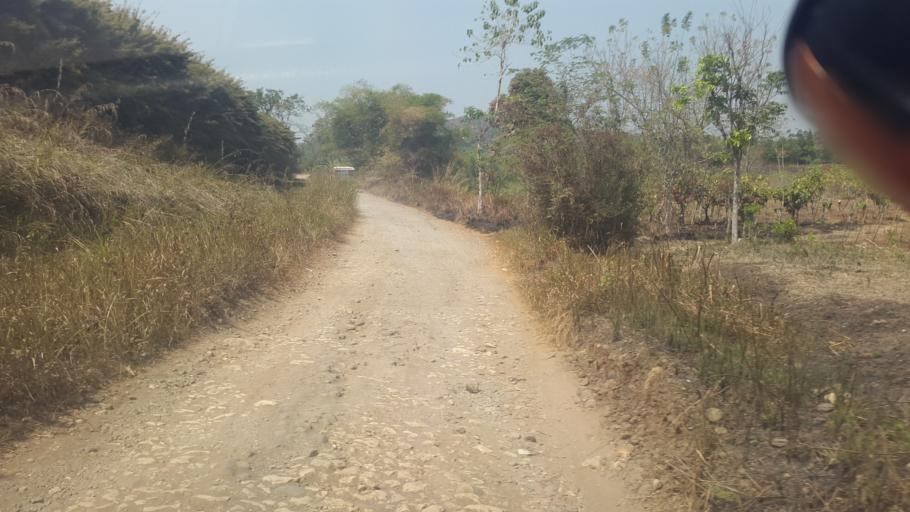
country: ID
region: West Java
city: Ciroyom
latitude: -7.0932
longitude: 106.8225
